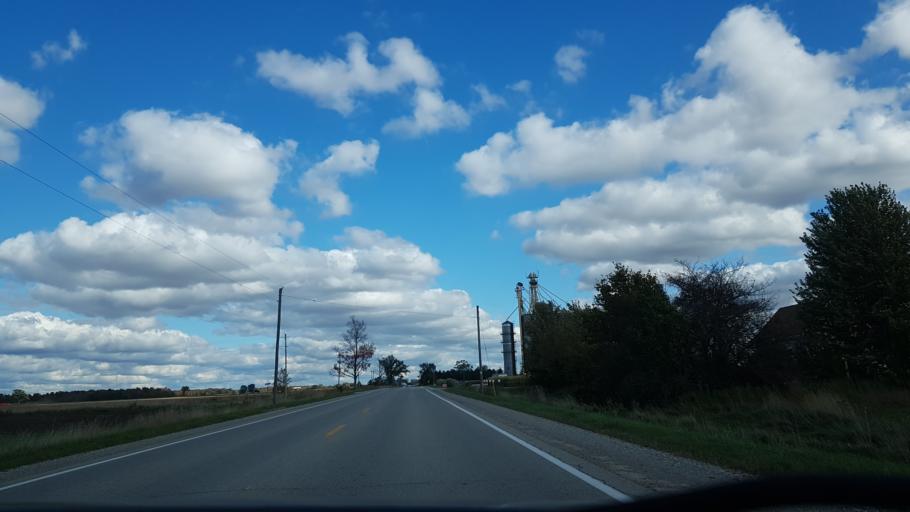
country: CA
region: Ontario
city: Lambton Shores
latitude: 43.2399
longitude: -81.7431
